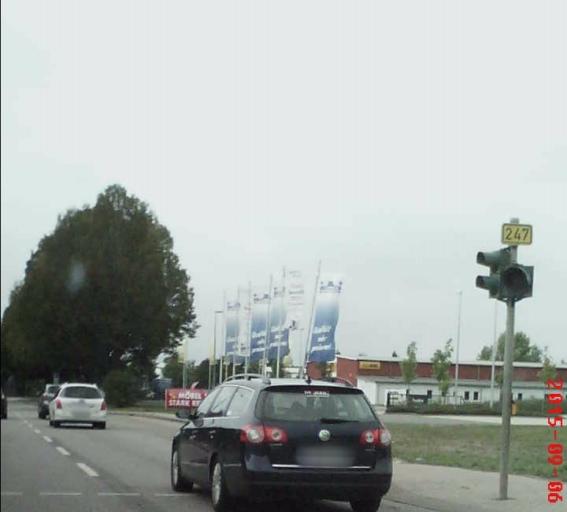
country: DE
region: Thuringia
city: Muehlhausen
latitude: 51.2167
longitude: 10.4602
